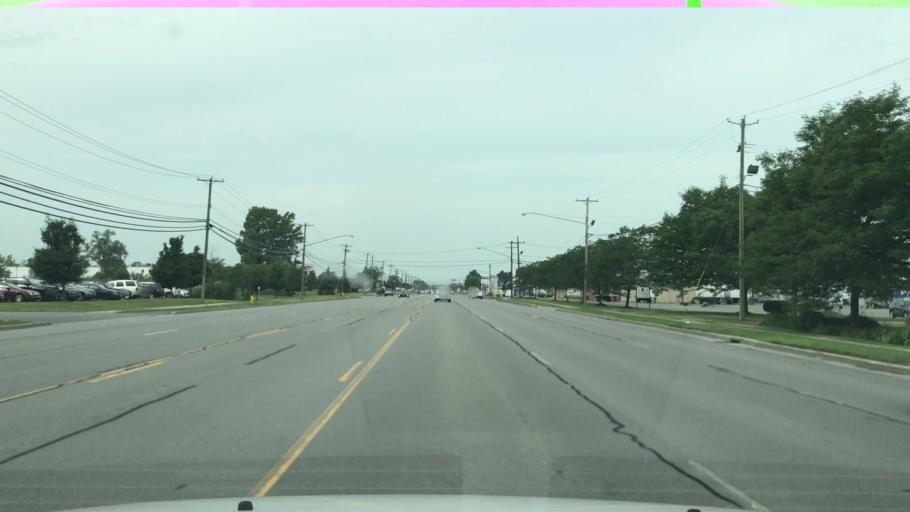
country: US
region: New York
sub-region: Erie County
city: Cheektowaga
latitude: 42.9095
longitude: -78.7331
